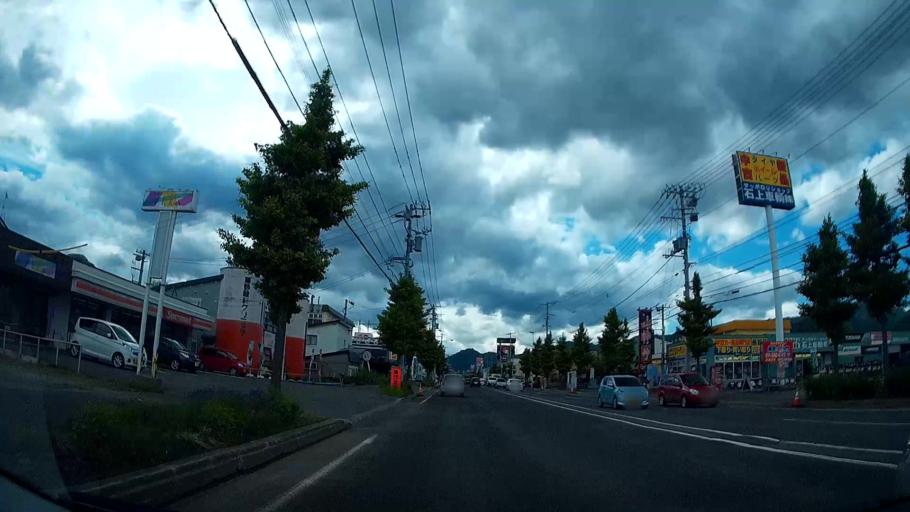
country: JP
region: Hokkaido
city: Sapporo
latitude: 42.9615
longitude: 141.3002
